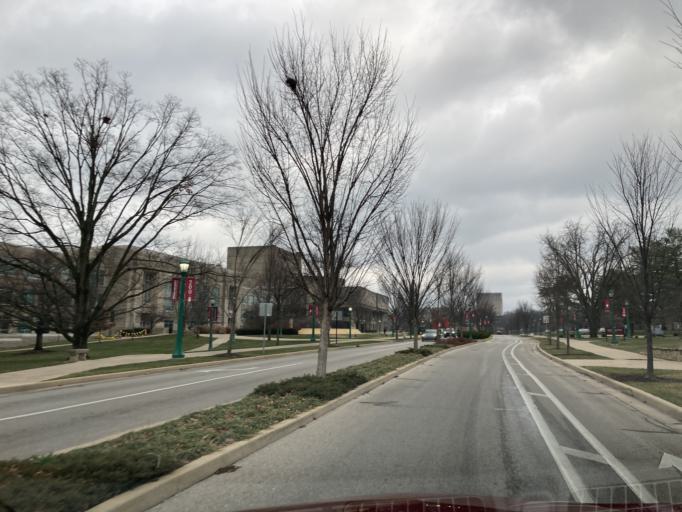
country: US
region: Indiana
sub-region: Monroe County
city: Bloomington
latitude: 39.1643
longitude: -86.5164
